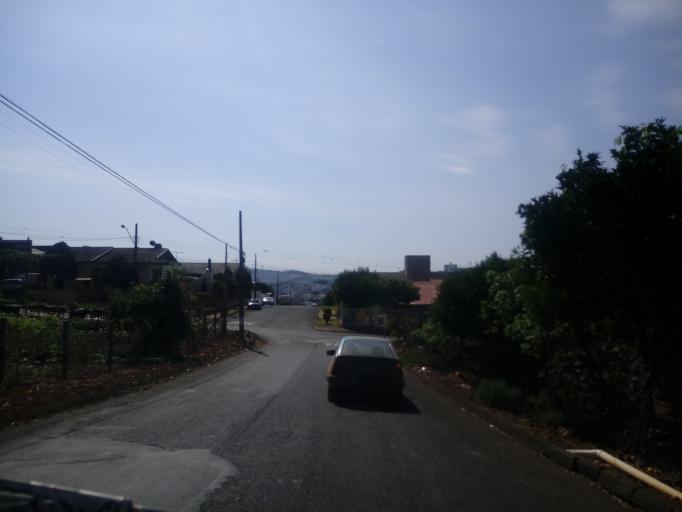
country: BR
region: Santa Catarina
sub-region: Chapeco
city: Chapeco
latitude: -27.0846
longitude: -52.6281
